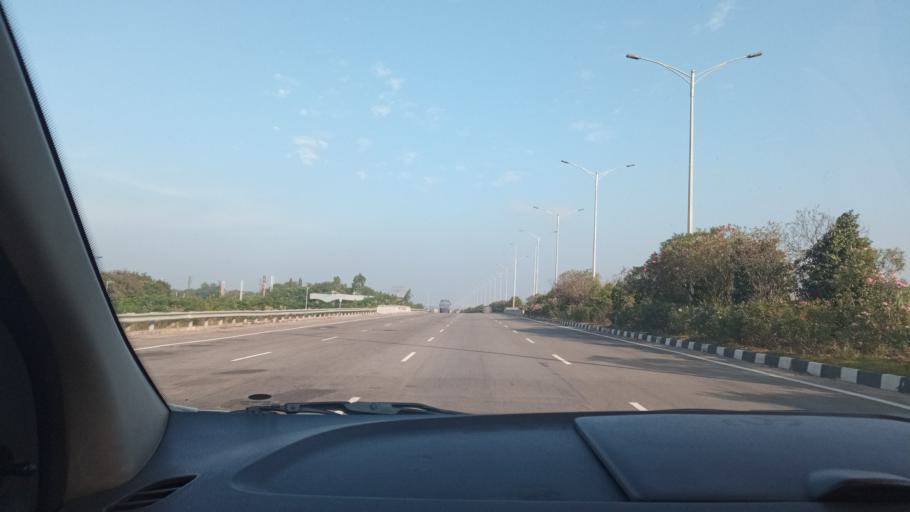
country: IN
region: Telangana
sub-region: Hyderabad
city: Hyderabad
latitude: 17.3486
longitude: 78.3605
